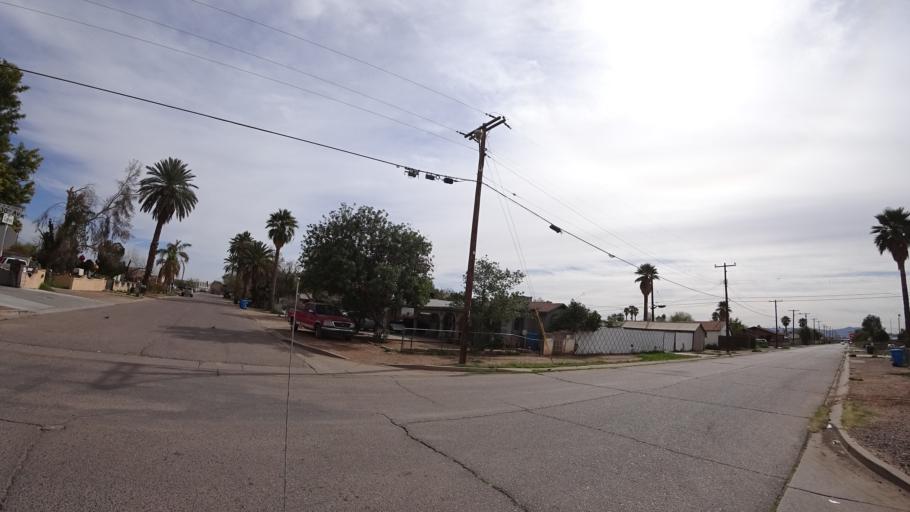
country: US
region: Arizona
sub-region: Maricopa County
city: Phoenix
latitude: 33.4723
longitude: -112.1237
